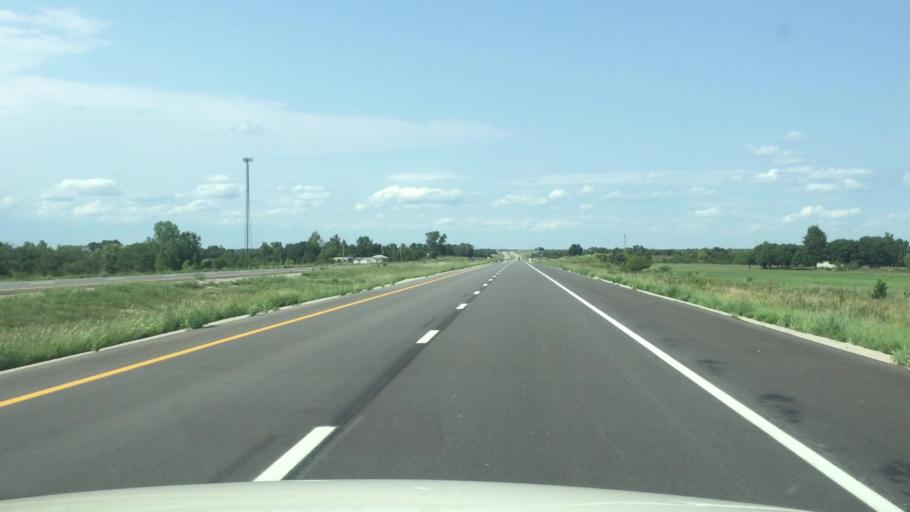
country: US
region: Kansas
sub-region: Linn County
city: La Cygne
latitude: 38.3708
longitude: -94.6874
